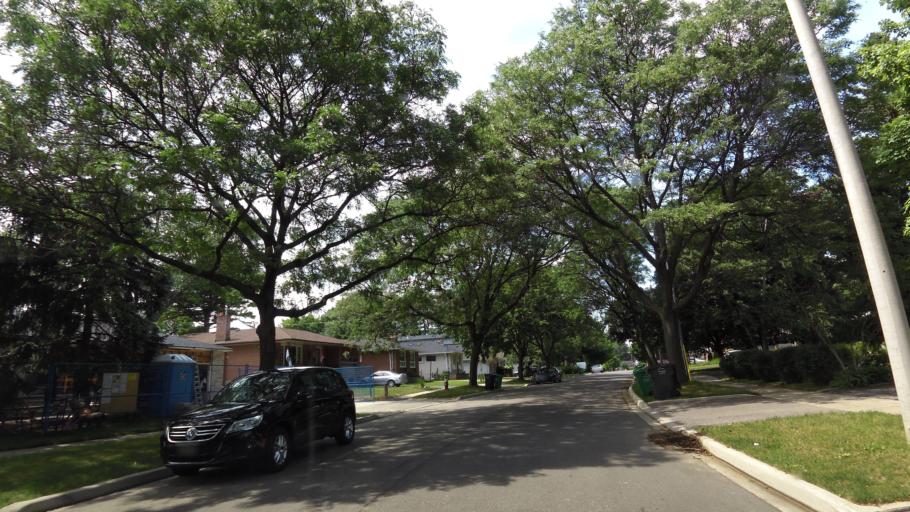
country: CA
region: Ontario
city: Etobicoke
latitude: 43.5884
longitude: -79.5650
